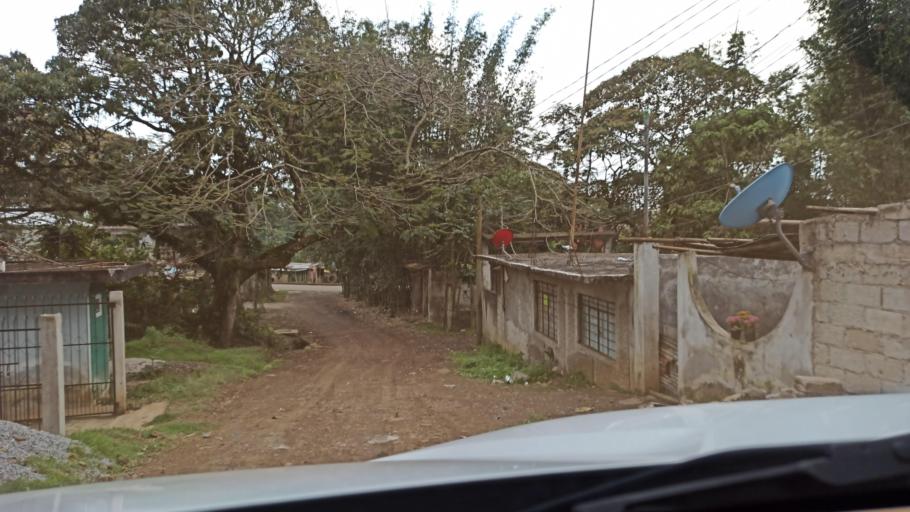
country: MX
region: Veracruz
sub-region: Fortin
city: Monte Salas
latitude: 18.9247
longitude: -97.0106
